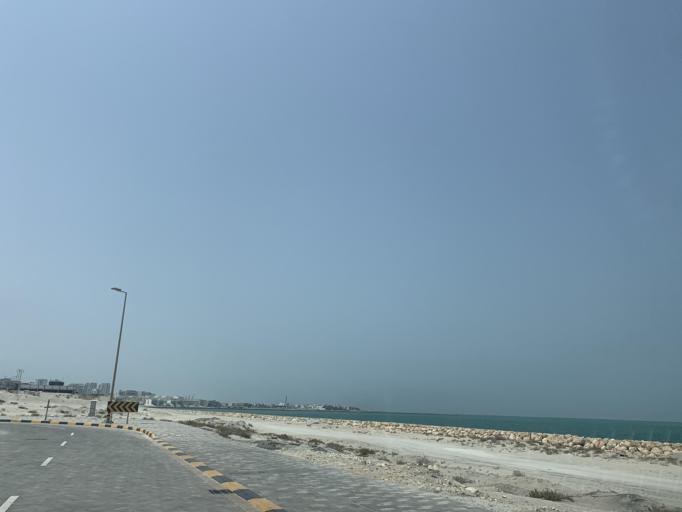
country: BH
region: Muharraq
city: Al Hadd
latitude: 26.2747
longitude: 50.6792
